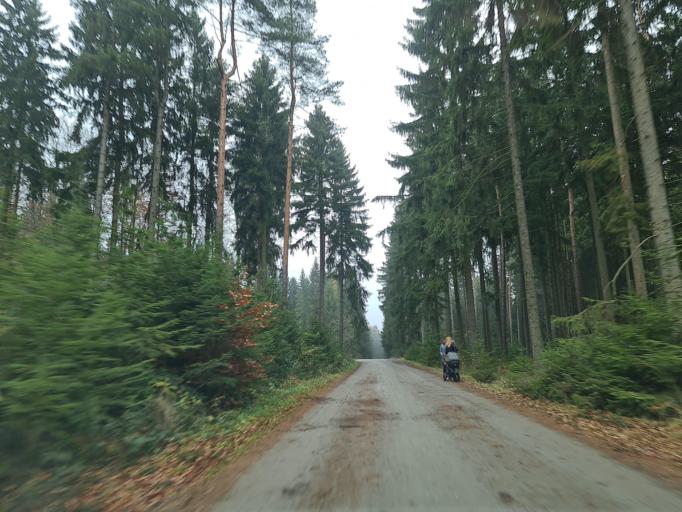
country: DE
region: Saxony
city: Mehltheuer
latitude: 50.5274
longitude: 12.0479
